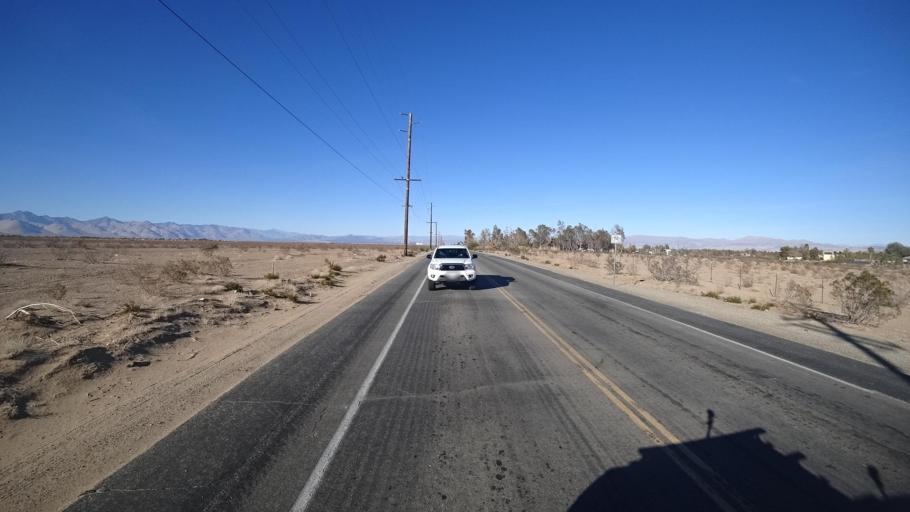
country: US
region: California
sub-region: Kern County
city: China Lake Acres
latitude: 35.6228
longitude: -117.7231
